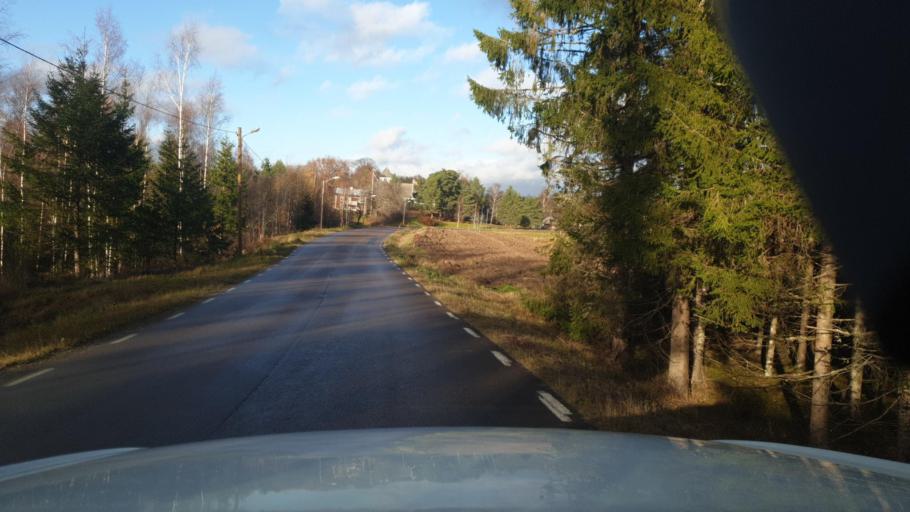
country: SE
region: Vaermland
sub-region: Karlstads Kommun
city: Edsvalla
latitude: 59.5657
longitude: 13.0538
